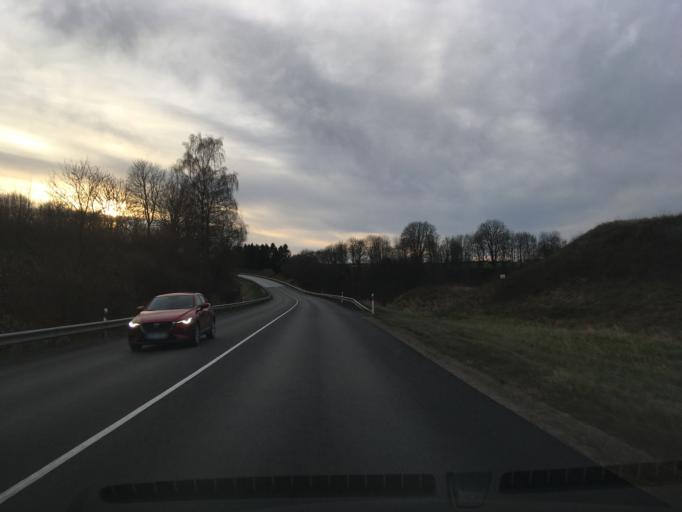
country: EE
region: Ida-Virumaa
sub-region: Aseri vald
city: Aseri
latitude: 59.4351
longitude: 26.7112
